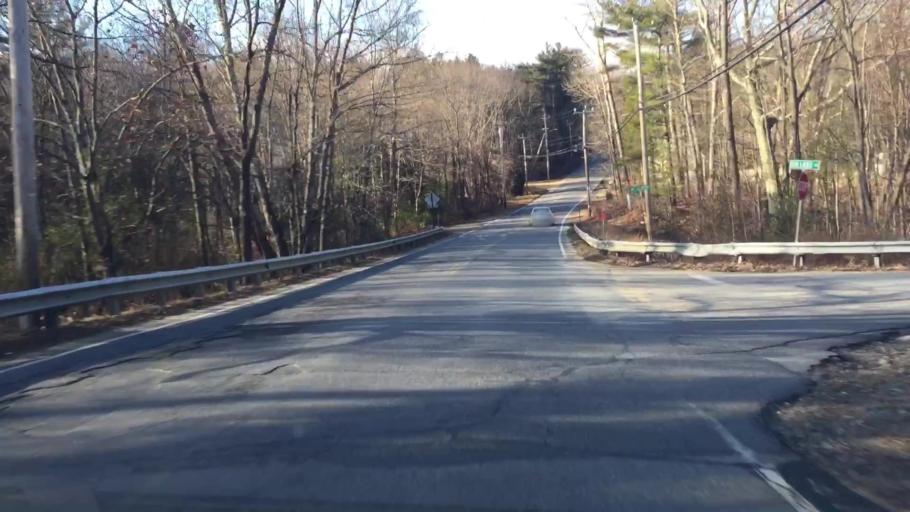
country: US
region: Massachusetts
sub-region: Worcester County
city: Princeton
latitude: 42.4440
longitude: -71.8470
